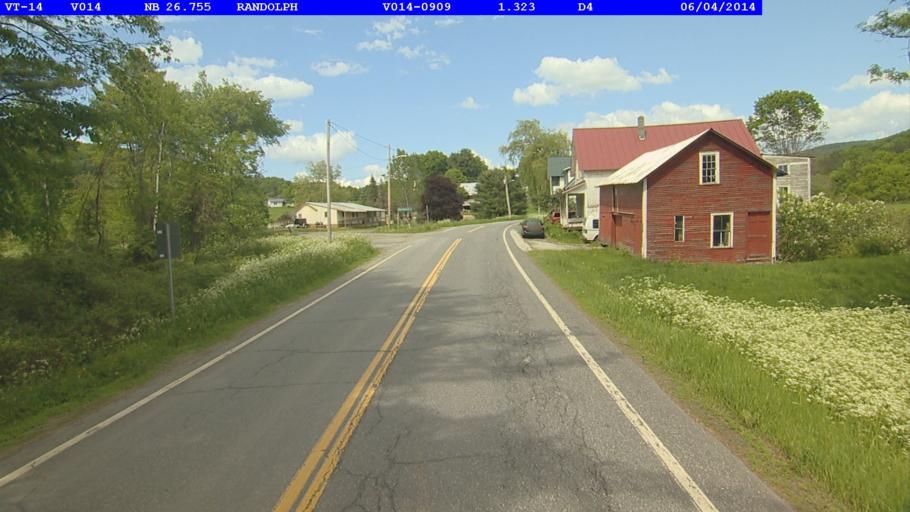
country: US
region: Vermont
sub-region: Orange County
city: Randolph
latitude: 43.8941
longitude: -72.5771
